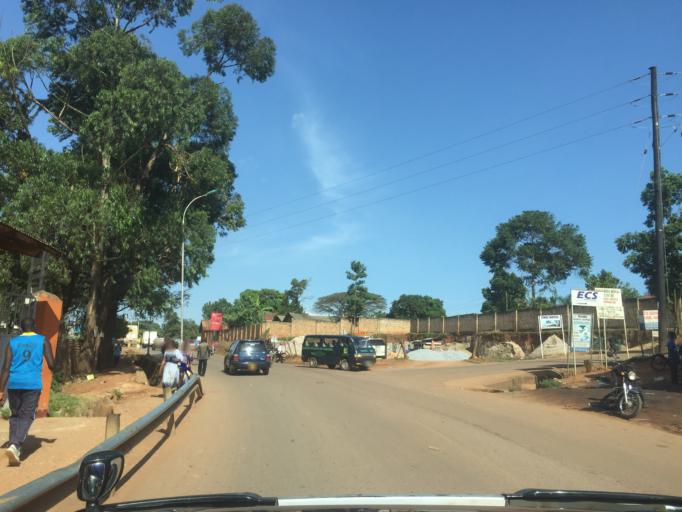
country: UG
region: Central Region
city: Kampala Central Division
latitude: 0.3813
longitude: 32.5634
